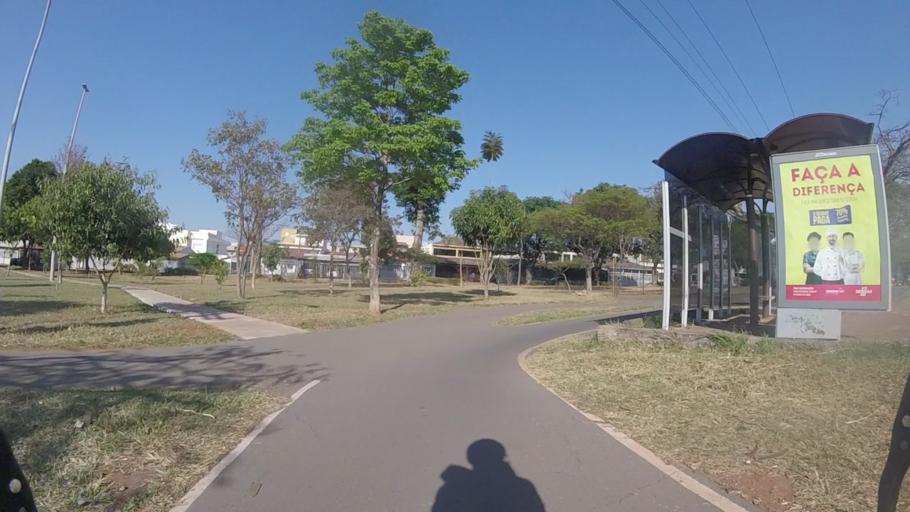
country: BR
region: Federal District
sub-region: Brasilia
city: Brasilia
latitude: -15.8354
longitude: -47.9744
